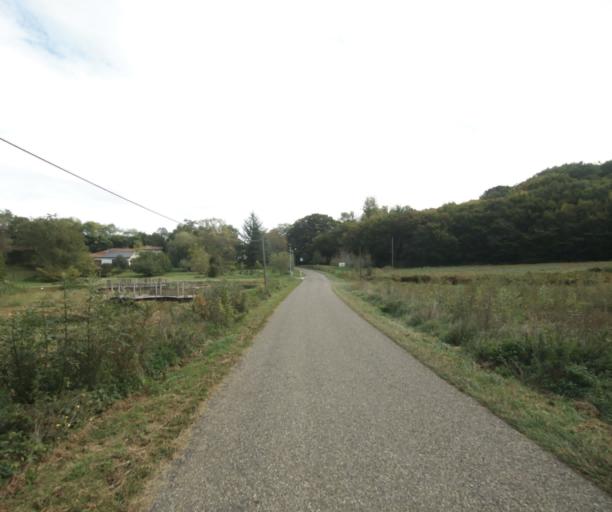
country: FR
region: Aquitaine
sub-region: Departement des Landes
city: Villeneuve-de-Marsan
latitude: 43.9007
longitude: -0.2184
